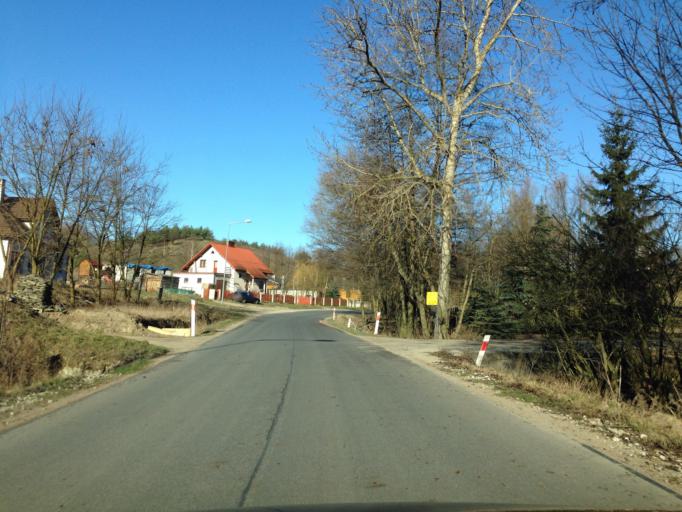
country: PL
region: Warmian-Masurian Voivodeship
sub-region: Powiat nowomiejski
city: Nowe Miasto Lubawskie
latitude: 53.4453
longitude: 19.5915
